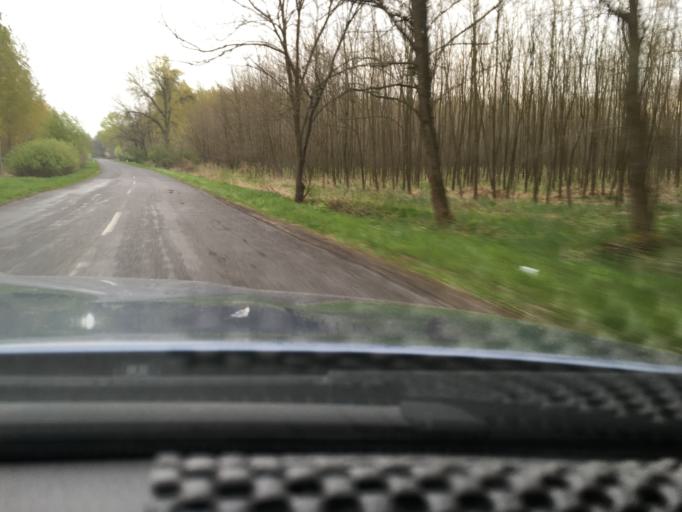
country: HU
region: Szabolcs-Szatmar-Bereg
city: Nyirlugos
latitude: 47.6962
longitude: 22.0679
